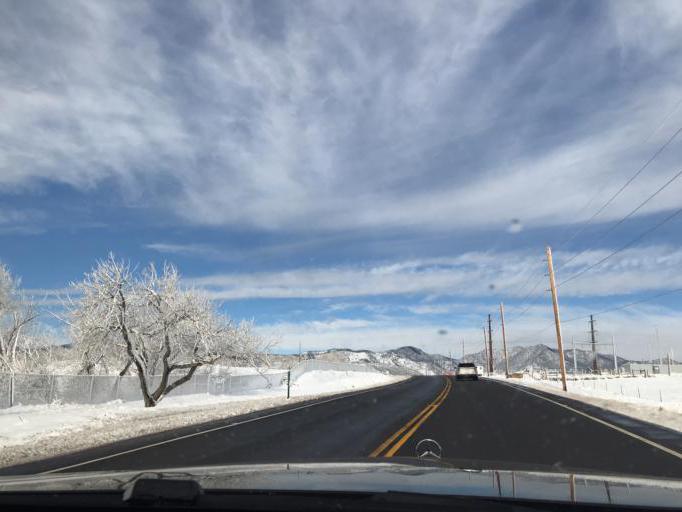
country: US
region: Colorado
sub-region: Boulder County
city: Superior
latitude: 39.8622
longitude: -105.1996
